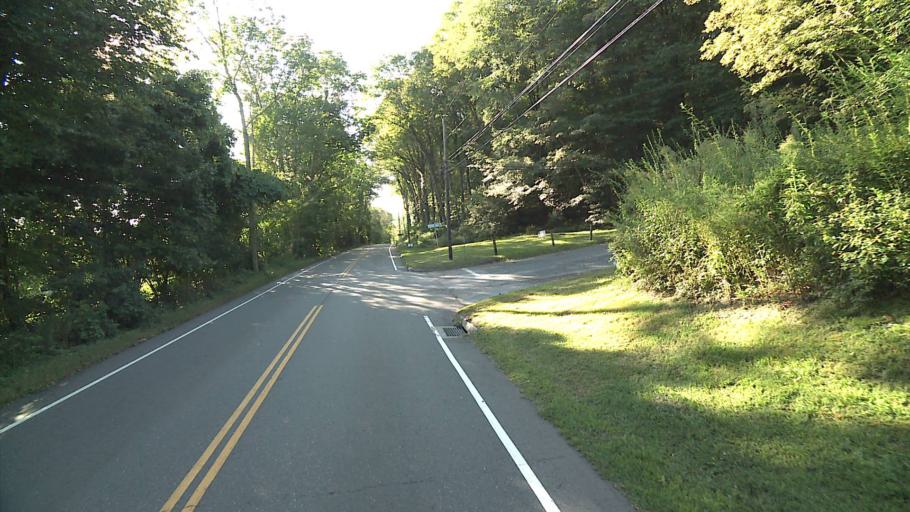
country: US
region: Connecticut
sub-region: New London County
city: Baltic
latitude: 41.6084
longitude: -72.1410
